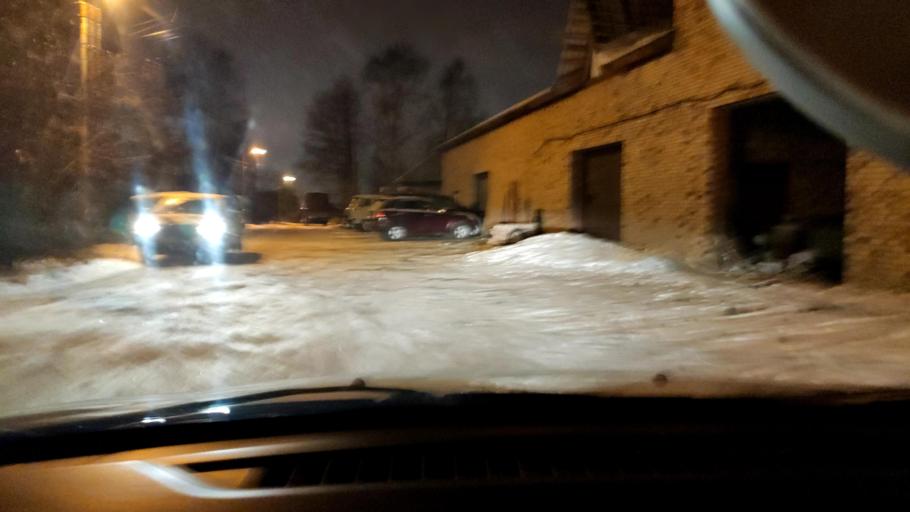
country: RU
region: Perm
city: Perm
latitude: 58.0221
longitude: 56.3313
